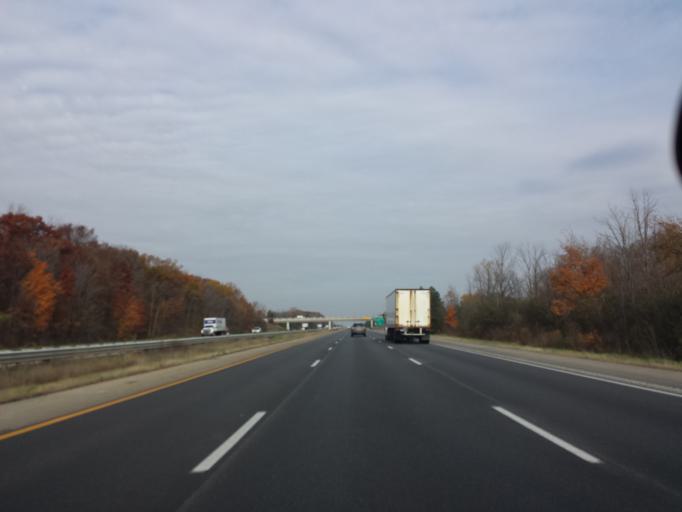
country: US
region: Michigan
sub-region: Genesee County
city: Beecher
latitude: 43.0723
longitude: -83.7625
